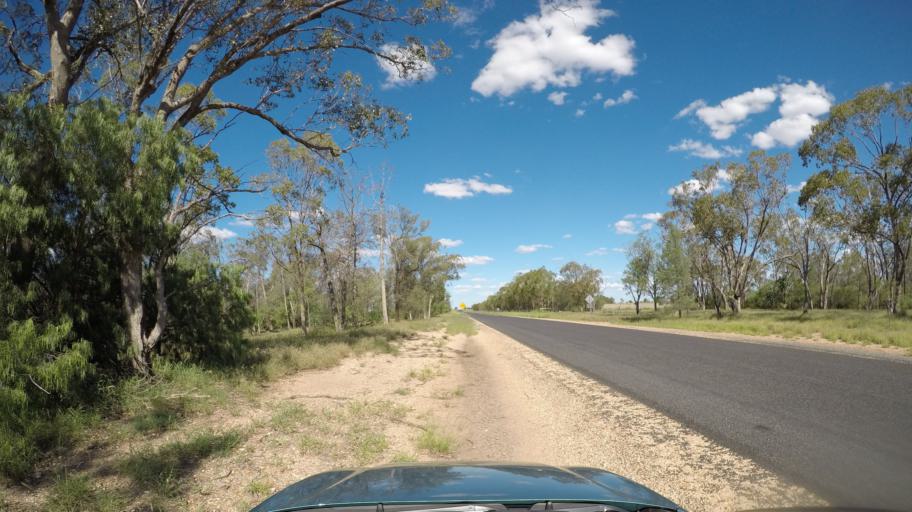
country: AU
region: Queensland
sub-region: Goondiwindi
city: Goondiwindi
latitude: -28.1588
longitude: 150.1210
